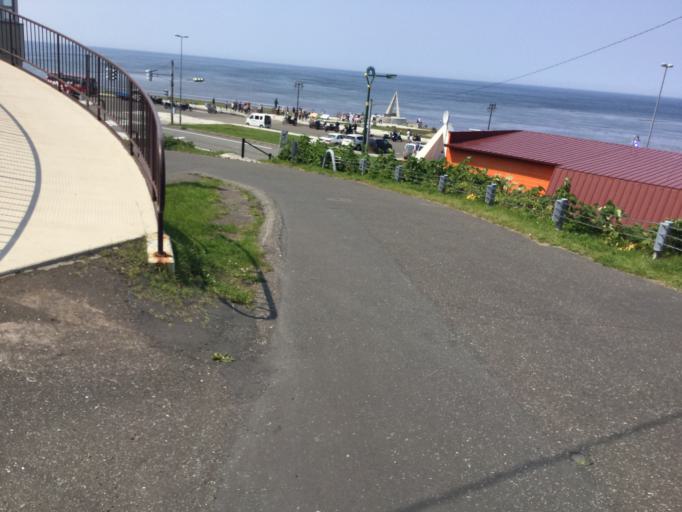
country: JP
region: Hokkaido
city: Makubetsu
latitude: 45.5218
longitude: 141.9374
